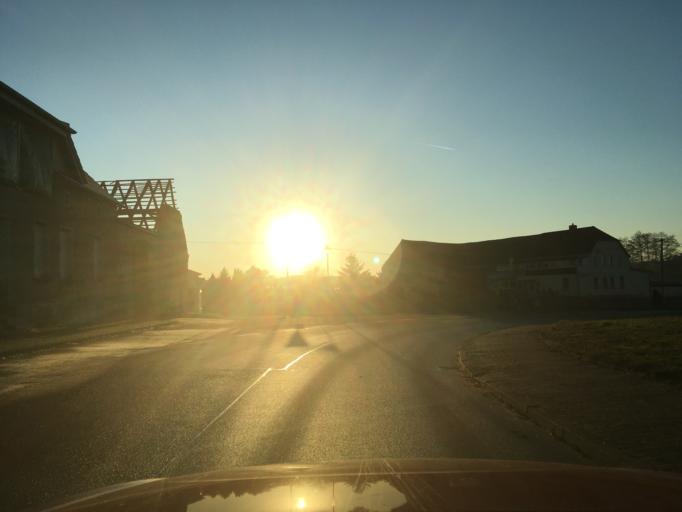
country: DE
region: Saxony-Anhalt
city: Klieken
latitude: 51.9236
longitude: 12.3226
